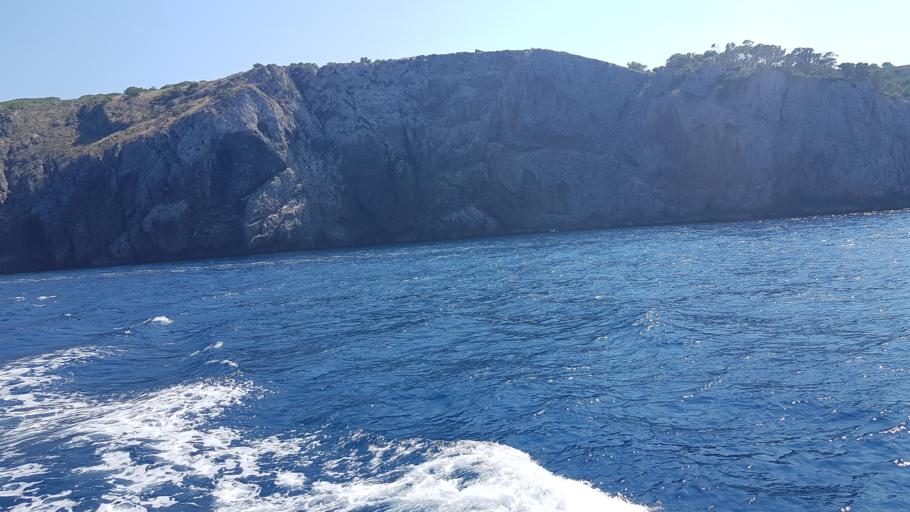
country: ES
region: Catalonia
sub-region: Provincia de Girona
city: Torroella de Montgri
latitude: 42.0720
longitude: 3.2099
